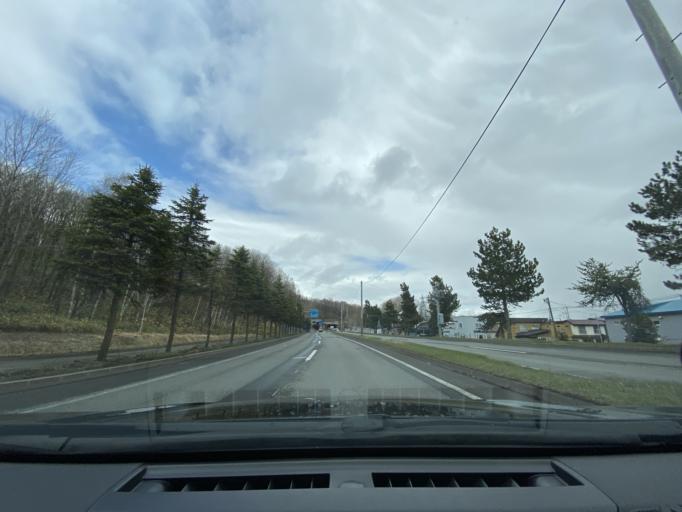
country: JP
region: Hokkaido
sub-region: Asahikawa-shi
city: Asahikawa
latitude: 43.8001
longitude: 142.3409
